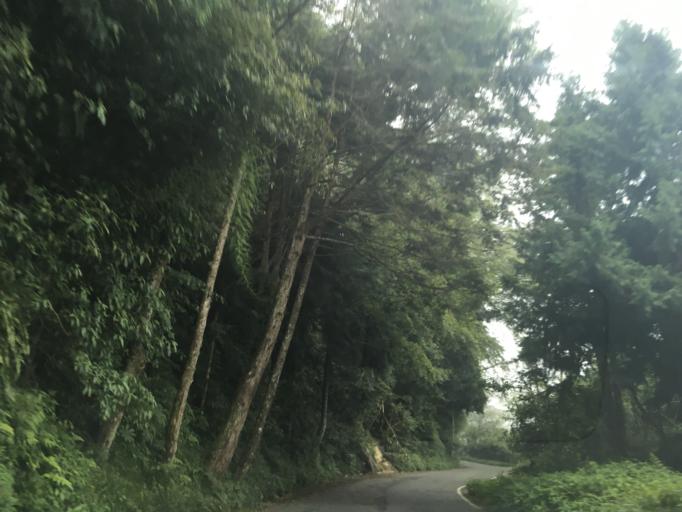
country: TW
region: Taiwan
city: Fengyuan
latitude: 24.2283
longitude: 120.9645
